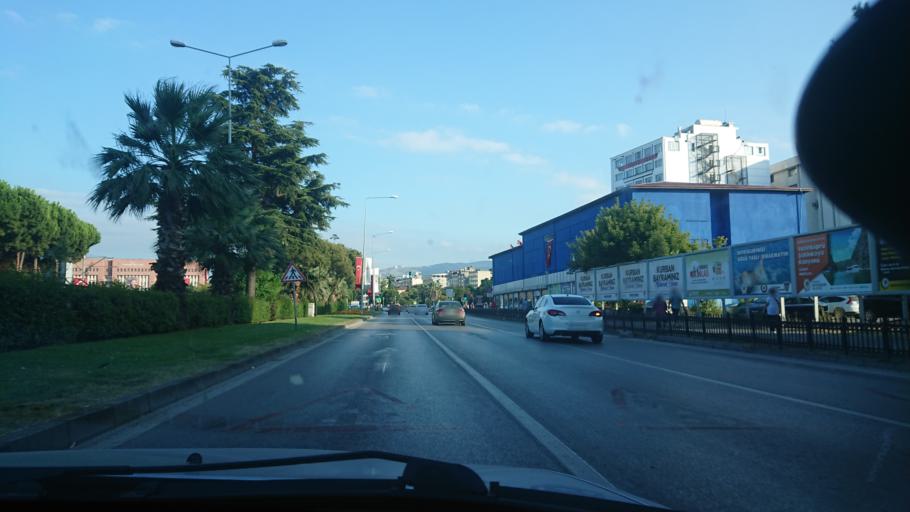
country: TR
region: Samsun
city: Samsun
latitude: 41.2920
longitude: 36.3351
